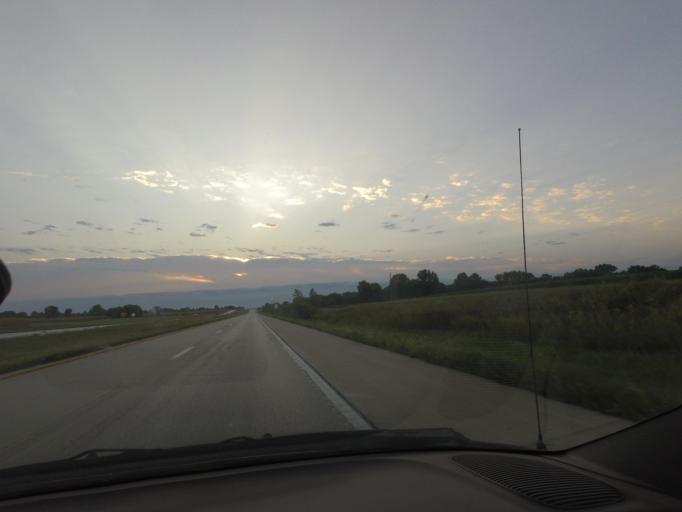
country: US
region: Missouri
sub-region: Macon County
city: Macon
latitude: 39.7507
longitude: -92.3825
